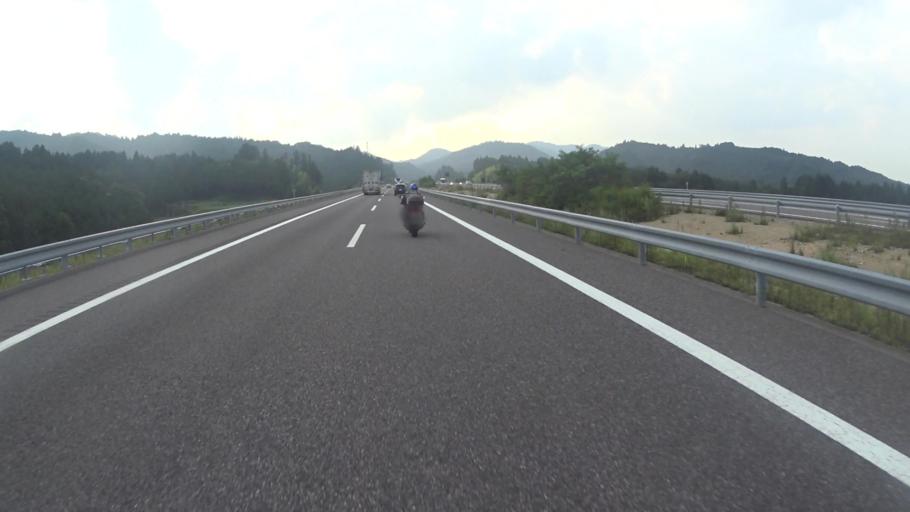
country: JP
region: Shiga Prefecture
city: Minakuchicho-matoba
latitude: 34.9144
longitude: 136.1520
